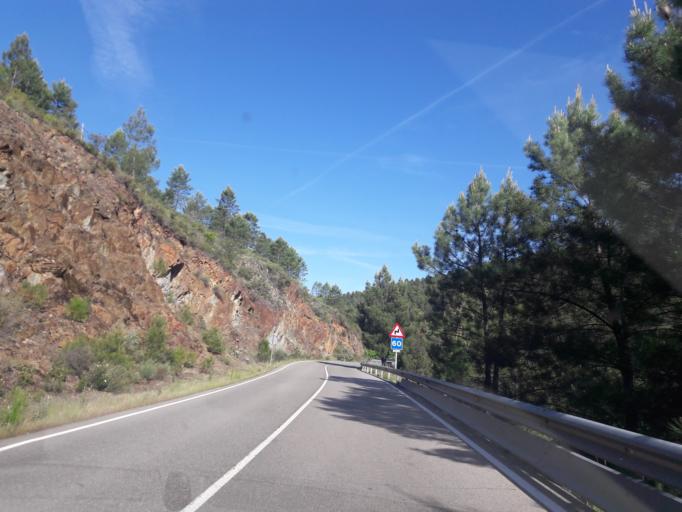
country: ES
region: Castille and Leon
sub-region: Provincia de Salamanca
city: Herguijuela de la Sierra
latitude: 40.4068
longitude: -6.0860
